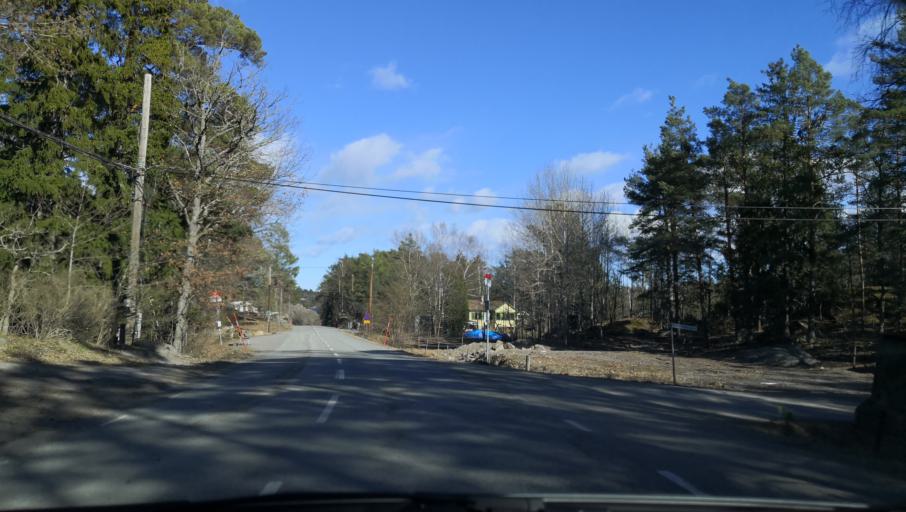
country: SE
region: Stockholm
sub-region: Varmdo Kommun
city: Holo
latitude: 59.3559
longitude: 18.6289
